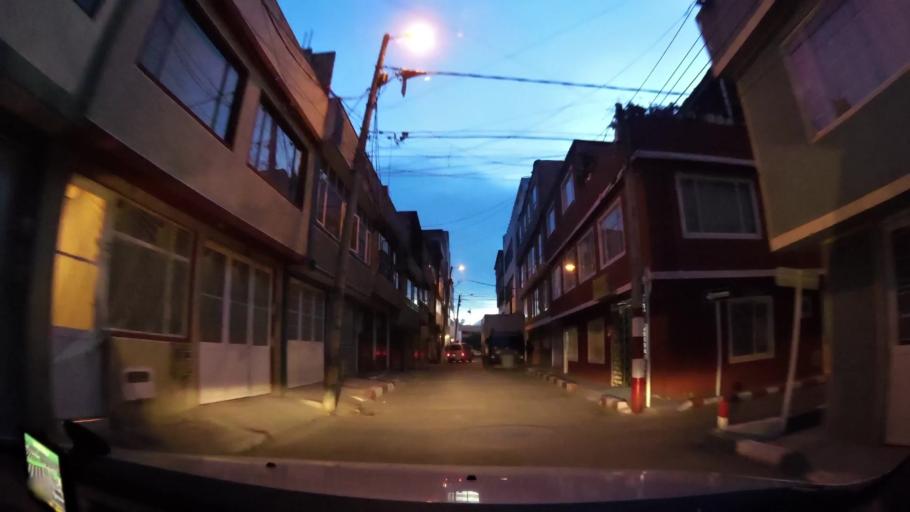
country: CO
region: Cundinamarca
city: Soacha
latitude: 4.6253
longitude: -74.1679
